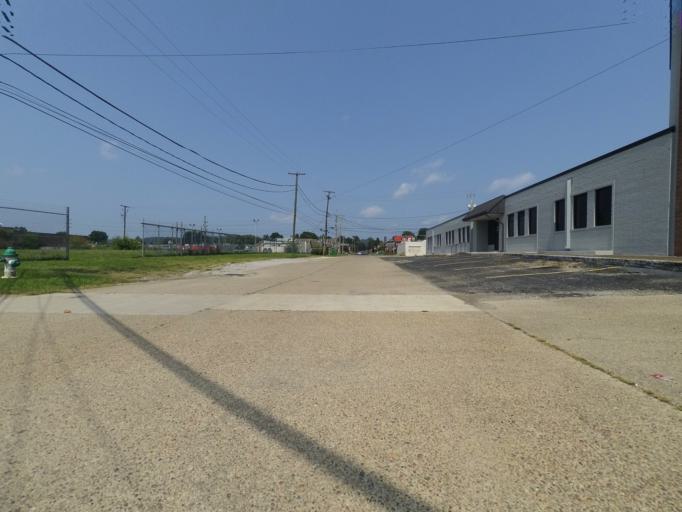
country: US
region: West Virginia
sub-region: Cabell County
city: Huntington
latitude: 38.4250
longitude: -82.4051
